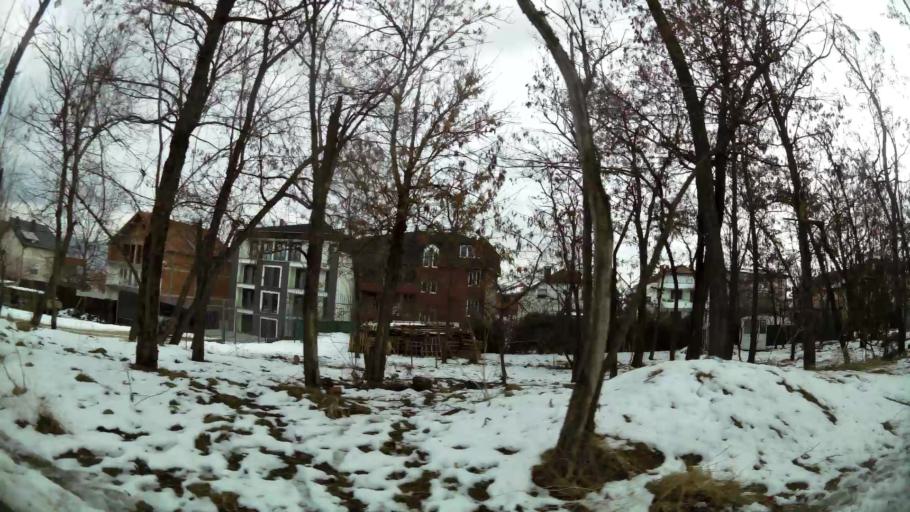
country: XK
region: Pristina
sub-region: Komuna e Prishtines
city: Pristina
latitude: 42.6698
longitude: 21.1531
